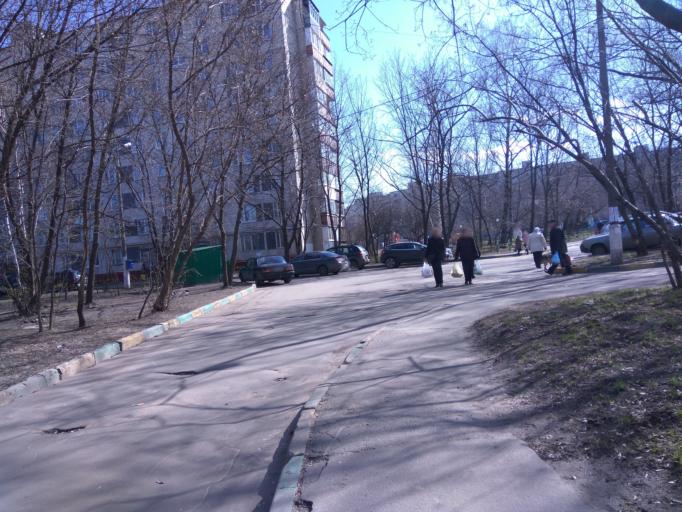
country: RU
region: Moscow
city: Ivanovskoye
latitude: 55.7741
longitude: 37.8367
